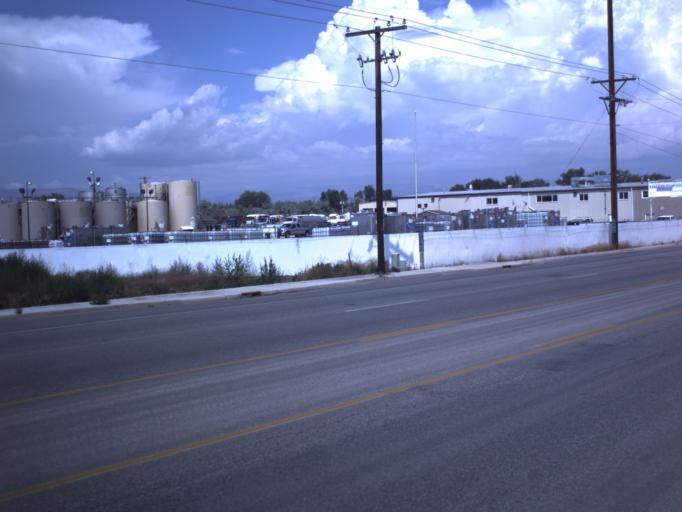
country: US
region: Utah
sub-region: Uintah County
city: Naples
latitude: 40.4310
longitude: -109.4994
